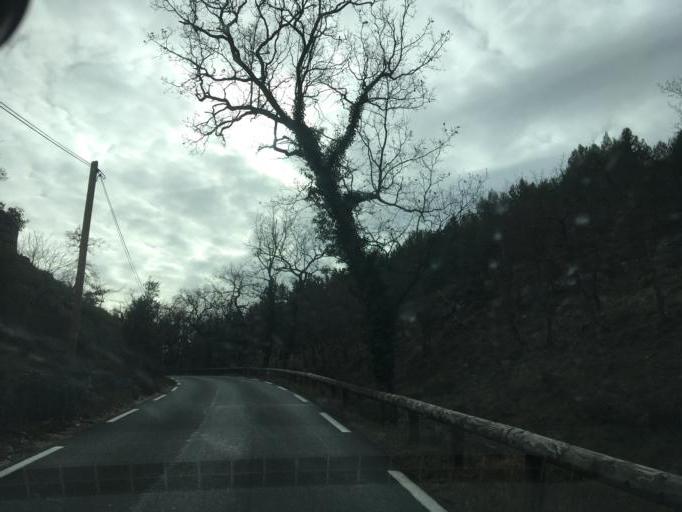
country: FR
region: Provence-Alpes-Cote d'Azur
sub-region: Departement du Var
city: Bras
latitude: 43.4556
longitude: 5.9704
